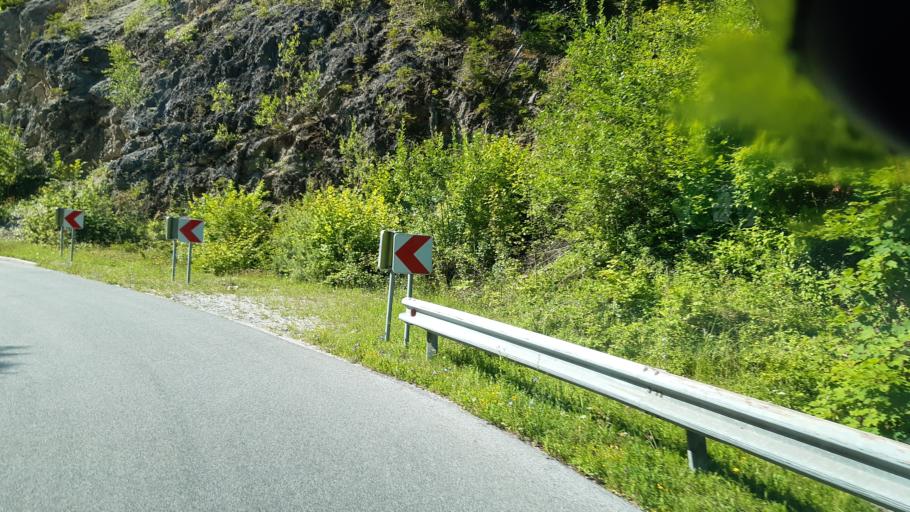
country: SI
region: Gornji Grad
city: Gornji Grad
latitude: 46.2140
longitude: 14.8071
